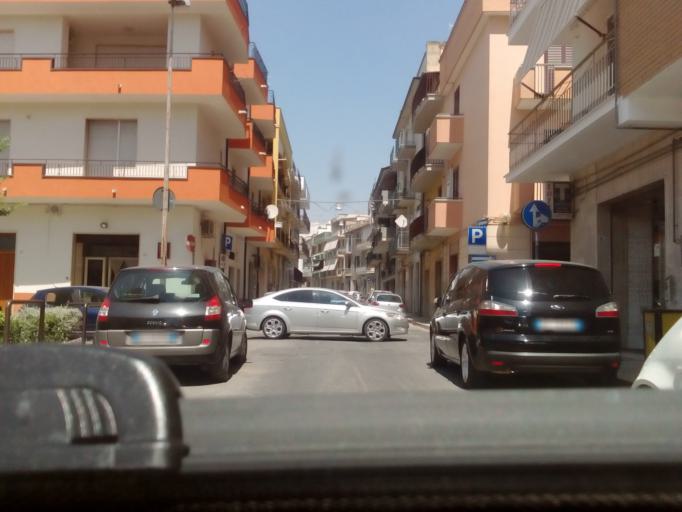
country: IT
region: Apulia
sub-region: Provincia di Bari
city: Gravina in Puglia
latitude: 40.8153
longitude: 16.4213
